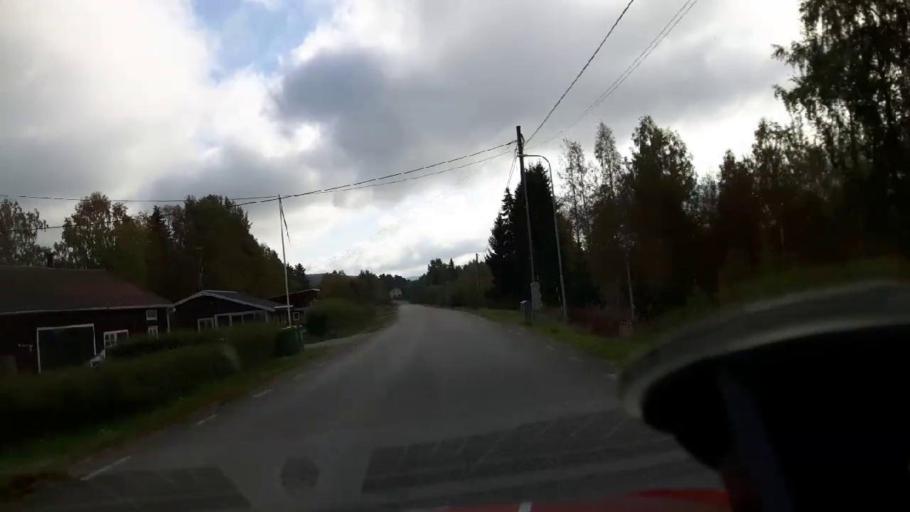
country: SE
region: Gaevleborg
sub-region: Ljusdals Kommun
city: Farila
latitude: 61.7868
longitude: 15.9236
